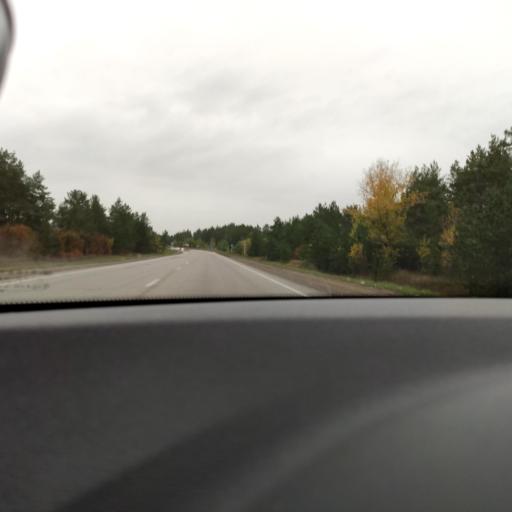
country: RU
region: Samara
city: Mirnyy
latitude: 53.5352
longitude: 50.3023
